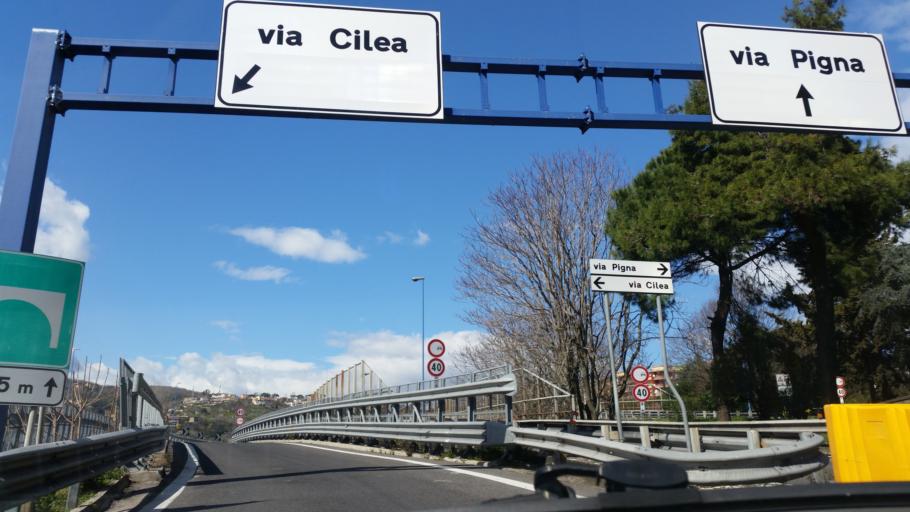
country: IT
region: Campania
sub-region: Provincia di Napoli
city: Napoli
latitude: 40.8442
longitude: 14.2185
